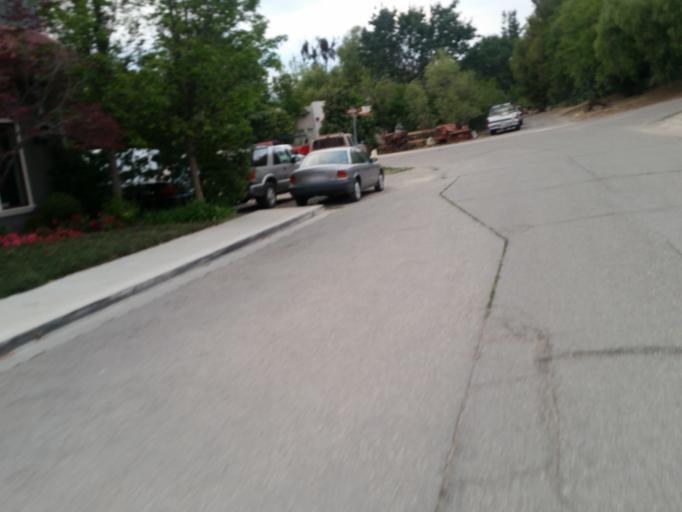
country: US
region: California
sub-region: Santa Barbara County
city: Los Olivos
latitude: 34.6662
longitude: -120.1138
